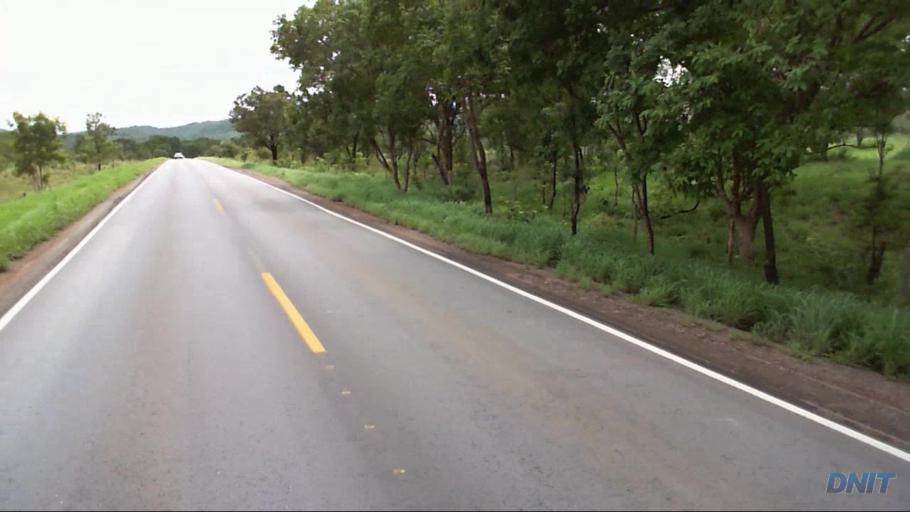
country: BR
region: Goias
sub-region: Padre Bernardo
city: Padre Bernardo
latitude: -15.4520
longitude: -48.2097
